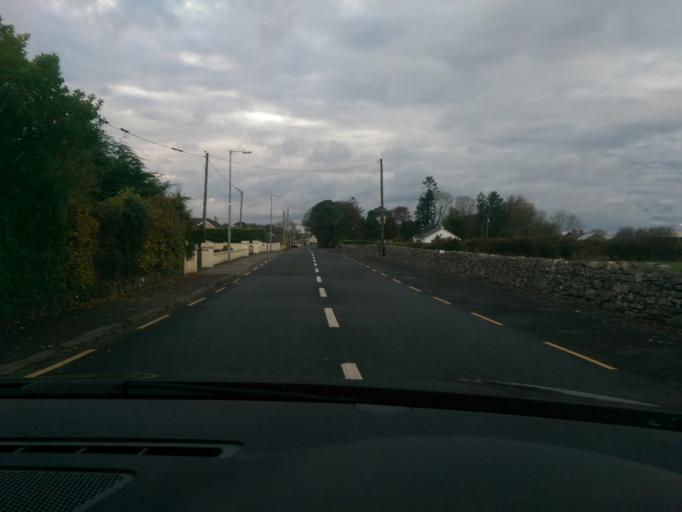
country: IE
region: Connaught
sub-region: County Galway
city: Athenry
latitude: 53.4215
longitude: -8.5639
